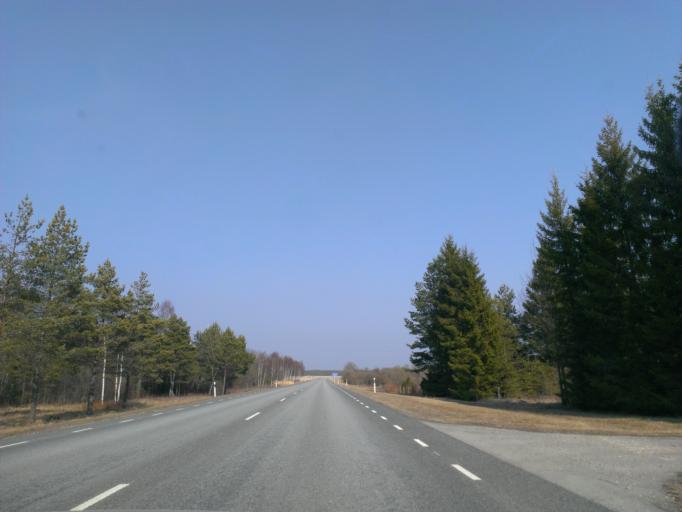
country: EE
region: Saare
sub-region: Orissaare vald
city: Orissaare
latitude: 58.5071
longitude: 22.8699
